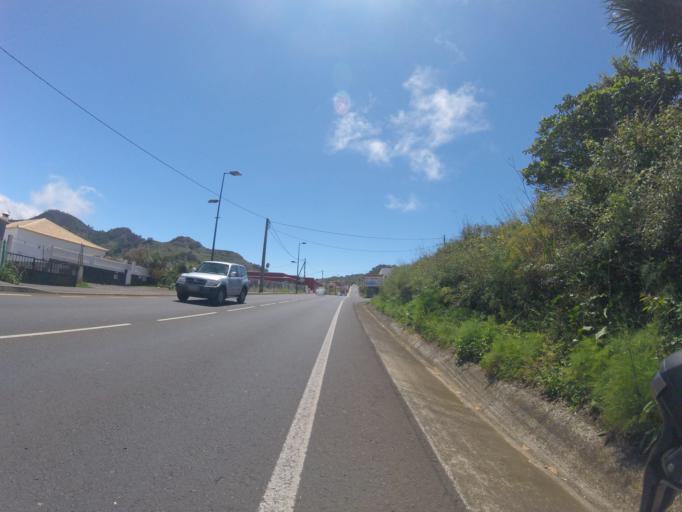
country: ES
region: Canary Islands
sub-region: Provincia de Santa Cruz de Tenerife
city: Tegueste
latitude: 28.5174
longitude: -16.3216
